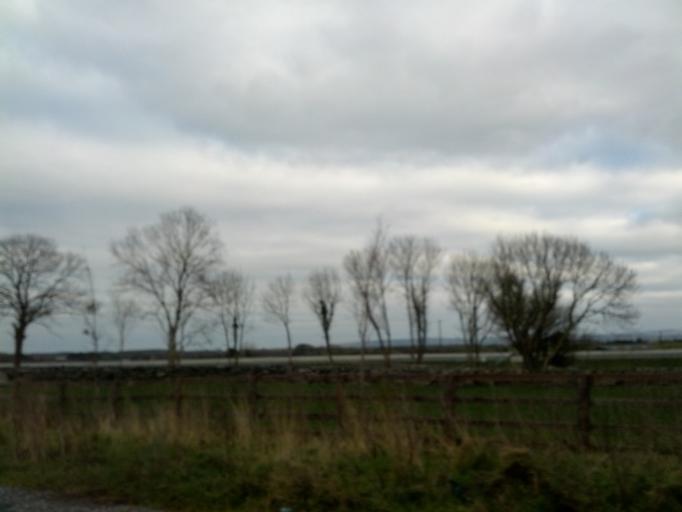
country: IE
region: Connaught
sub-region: County Galway
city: Gort
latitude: 53.1674
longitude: -8.8519
